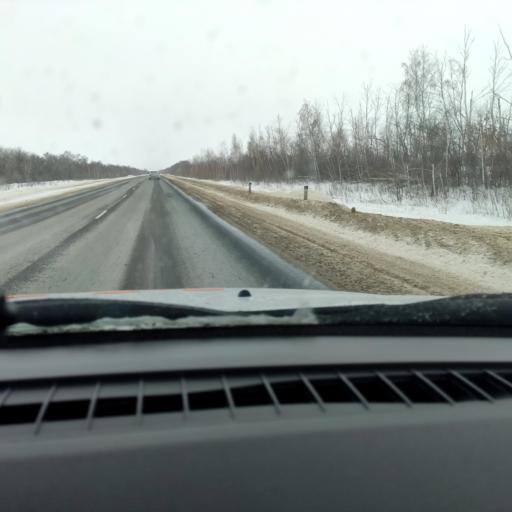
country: RU
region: Samara
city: Dubovyy Umet
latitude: 52.8861
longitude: 50.4211
